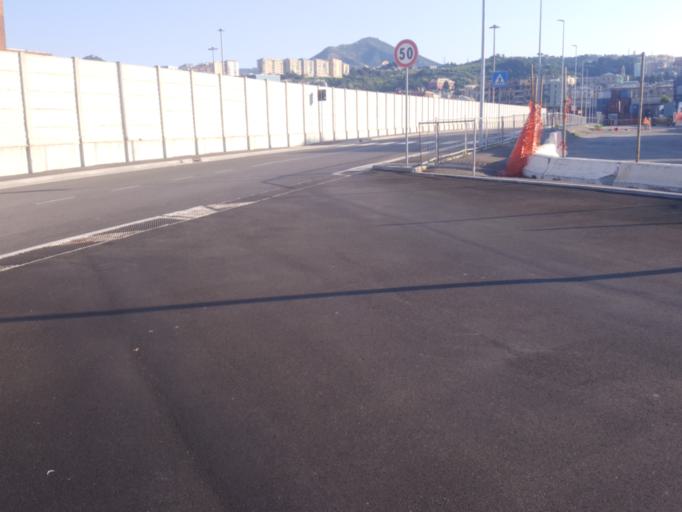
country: IT
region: Liguria
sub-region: Provincia di Genova
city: San Teodoro
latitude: 44.4095
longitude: 8.8713
